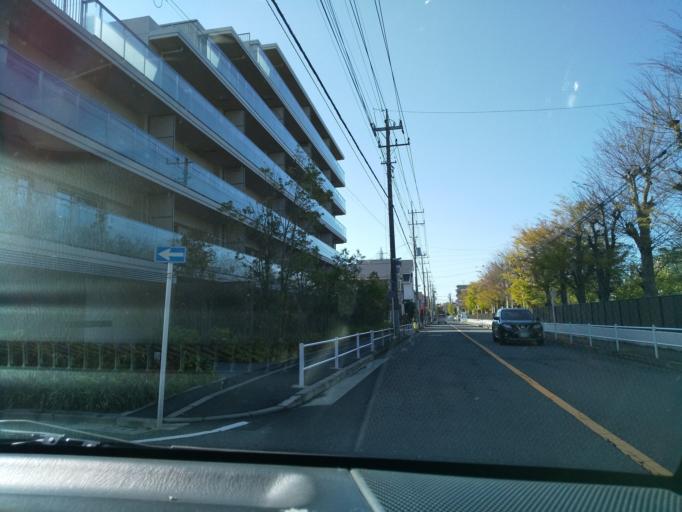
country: JP
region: Tokyo
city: Hino
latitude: 35.6921
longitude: 139.4345
